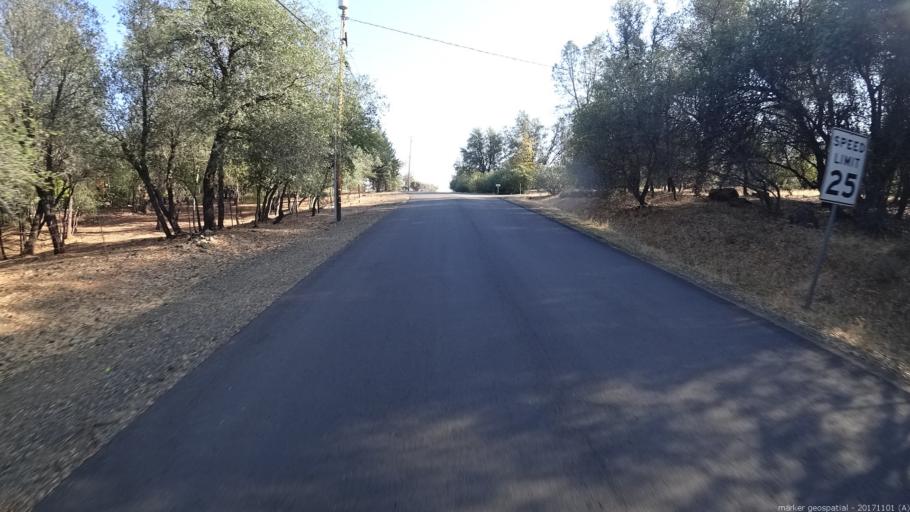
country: US
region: California
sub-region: Shasta County
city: Shasta Lake
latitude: 40.6764
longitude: -122.3007
